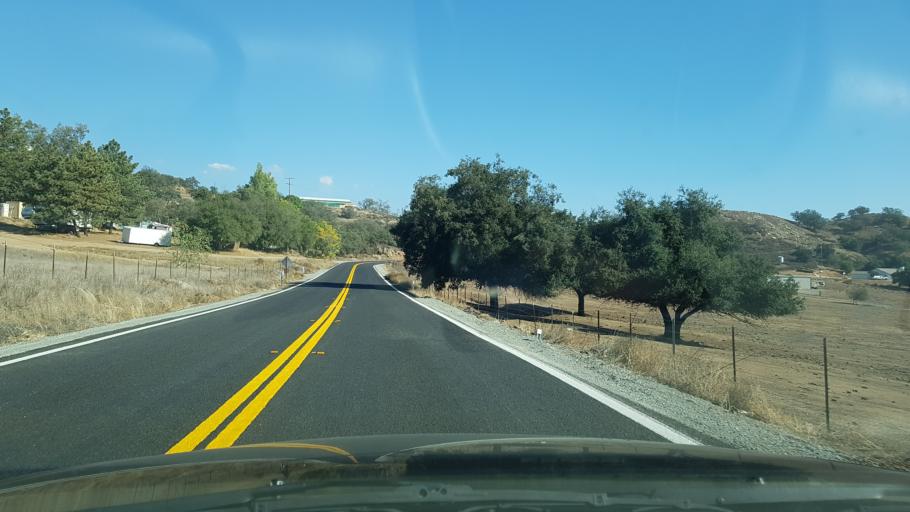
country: US
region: California
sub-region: San Diego County
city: San Diego Country Estates
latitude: 33.0714
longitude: -116.7668
